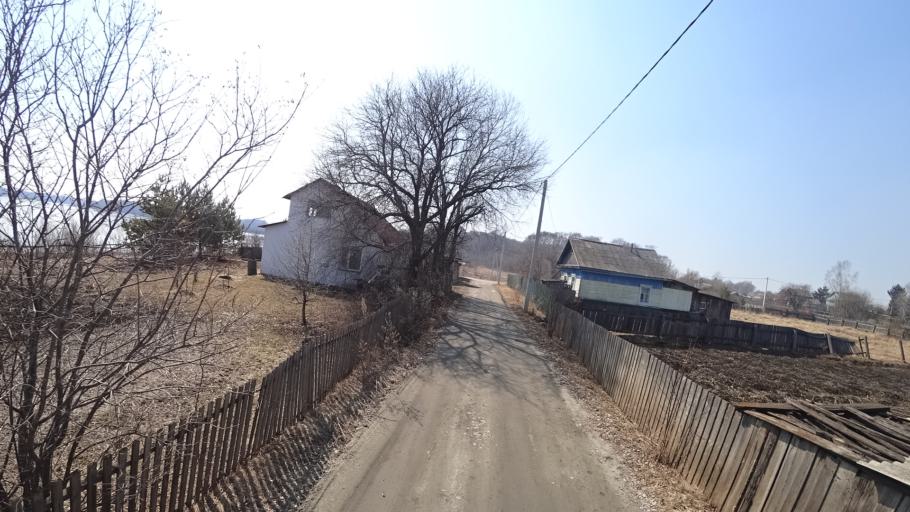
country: RU
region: Amur
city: Novobureyskiy
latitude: 49.7764
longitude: 129.8499
